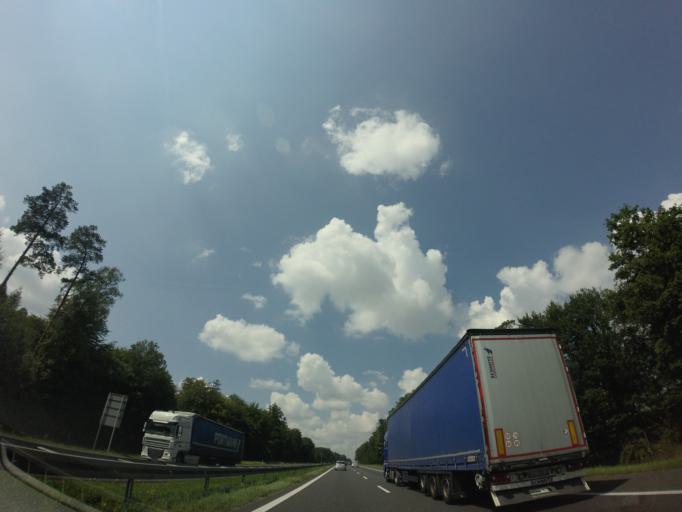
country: PL
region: Opole Voivodeship
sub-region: Powiat strzelecki
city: Ujazd
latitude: 50.4293
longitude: 18.3784
